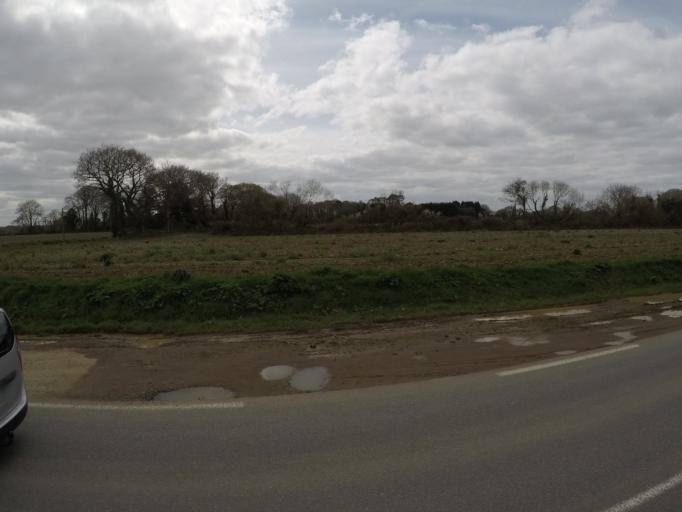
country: FR
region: Brittany
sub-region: Departement des Cotes-d'Armor
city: Plouha
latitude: 48.7055
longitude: -2.9539
